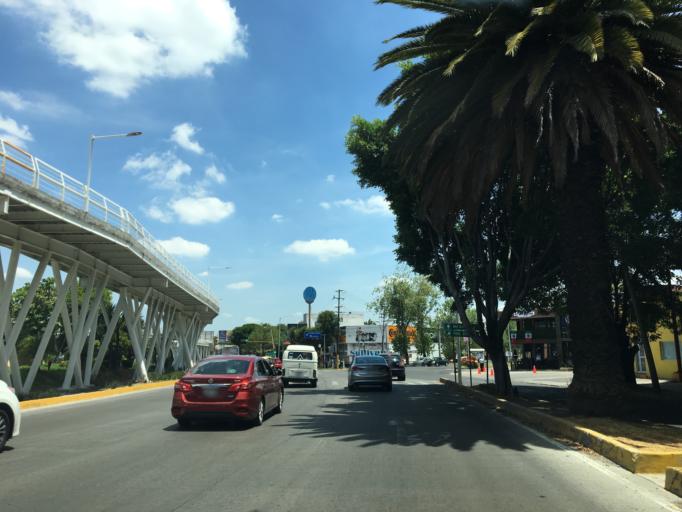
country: MX
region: Puebla
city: Puebla
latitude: 19.0630
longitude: -98.2214
